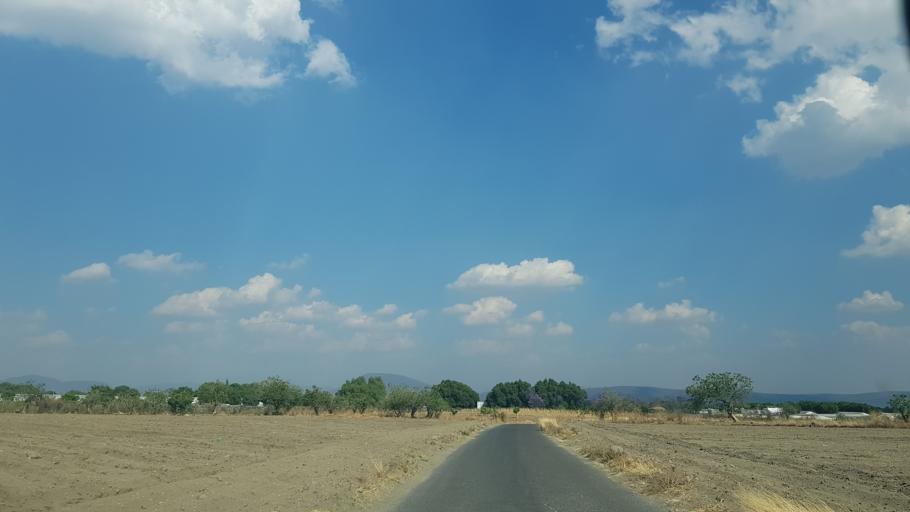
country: MX
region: Puebla
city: Atlixco
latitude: 18.8844
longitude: -98.4934
